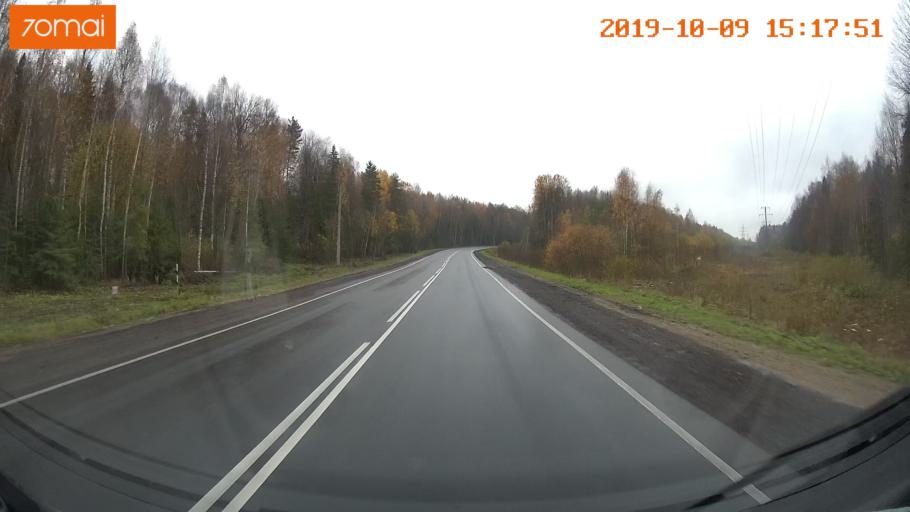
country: RU
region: Kostroma
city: Susanino
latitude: 58.0929
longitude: 41.5813
